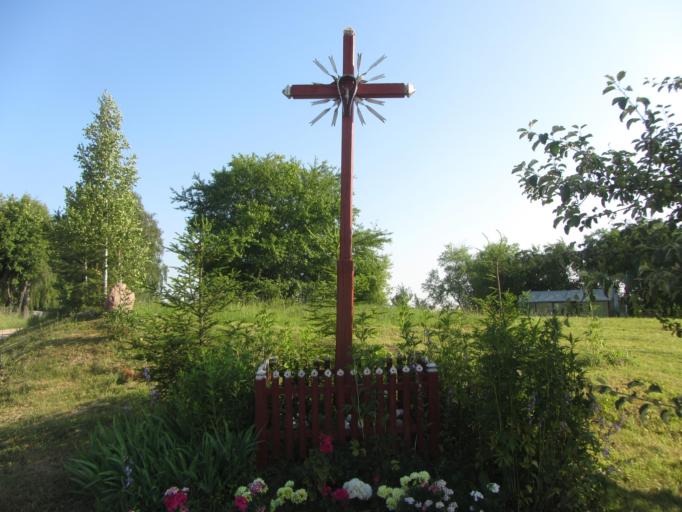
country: LT
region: Alytaus apskritis
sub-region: Alytus
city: Alytus
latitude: 54.2993
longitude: 23.9299
